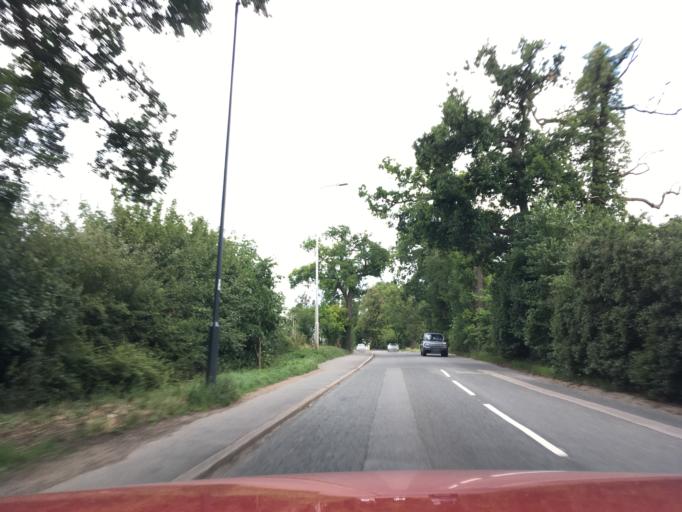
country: GB
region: England
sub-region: Warwickshire
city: Nuneaton
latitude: 52.5417
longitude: -1.4676
